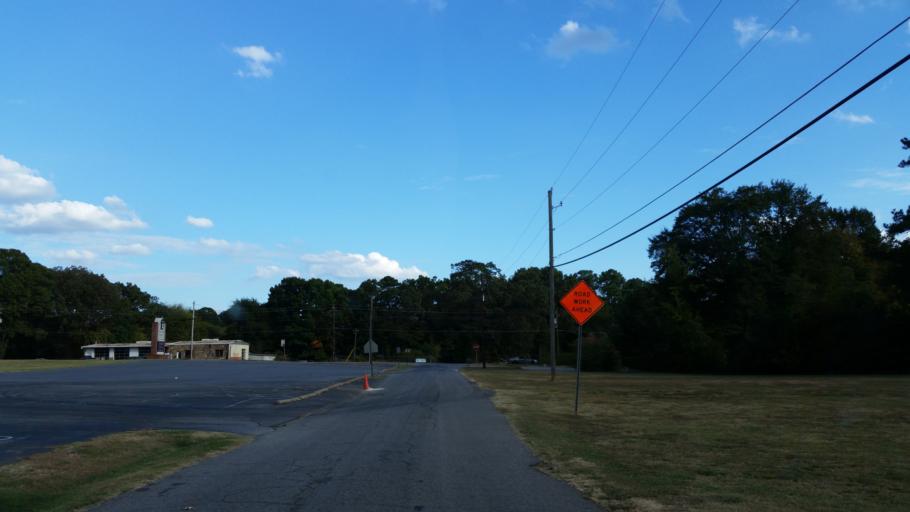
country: US
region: Georgia
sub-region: Bartow County
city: Cartersville
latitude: 34.2117
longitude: -84.7980
